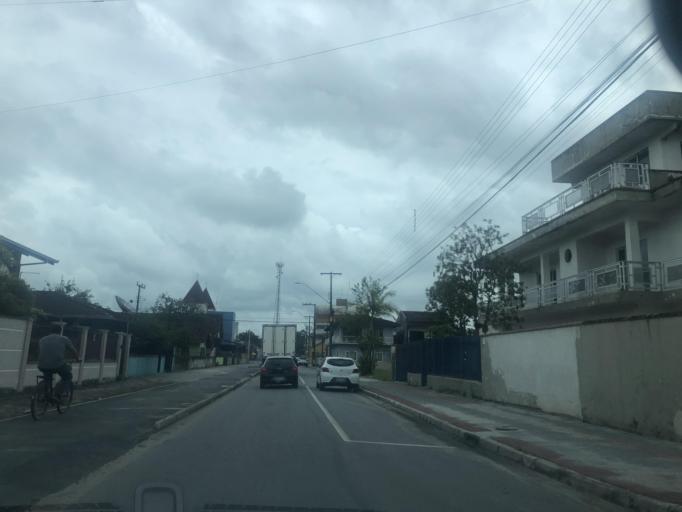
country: BR
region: Santa Catarina
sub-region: Joinville
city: Joinville
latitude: -26.3692
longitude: -48.7212
